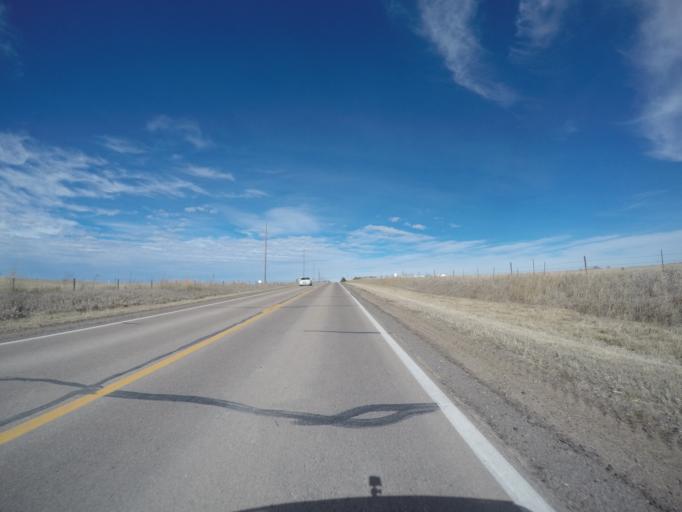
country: US
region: Nebraska
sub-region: Franklin County
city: Franklin
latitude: 40.1149
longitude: -98.9524
